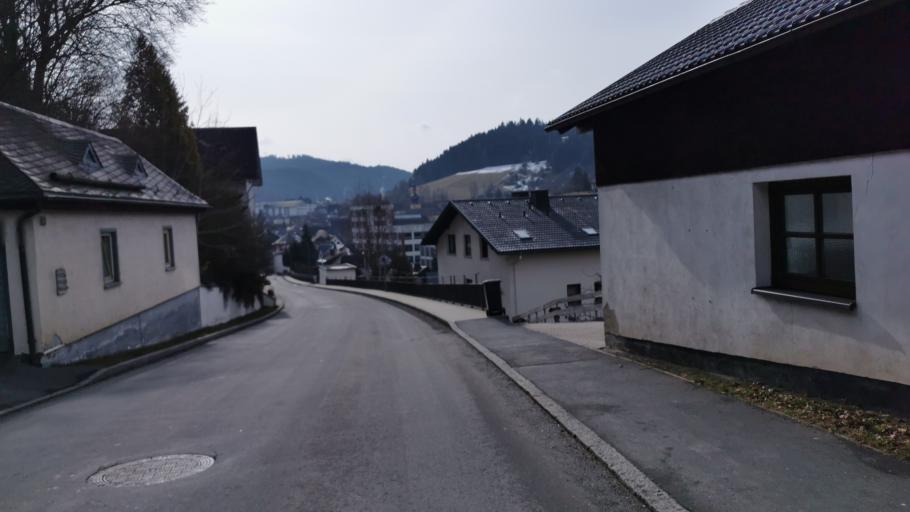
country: DE
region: Bavaria
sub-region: Upper Franconia
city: Ludwigsstadt
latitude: 50.4885
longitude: 11.3865
